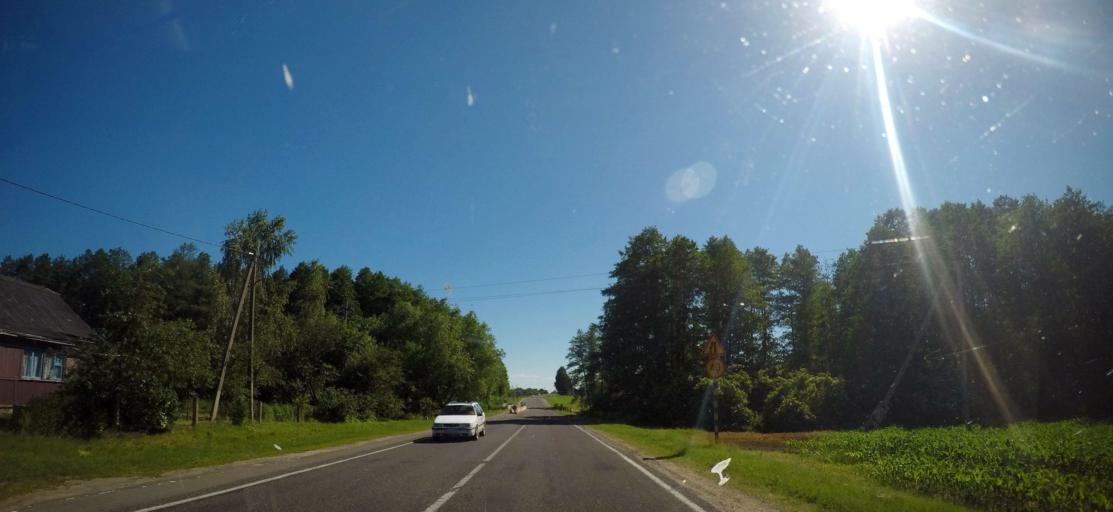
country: BY
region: Grodnenskaya
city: Vyalikaya Byerastavitsa
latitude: 53.1763
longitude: 23.9995
